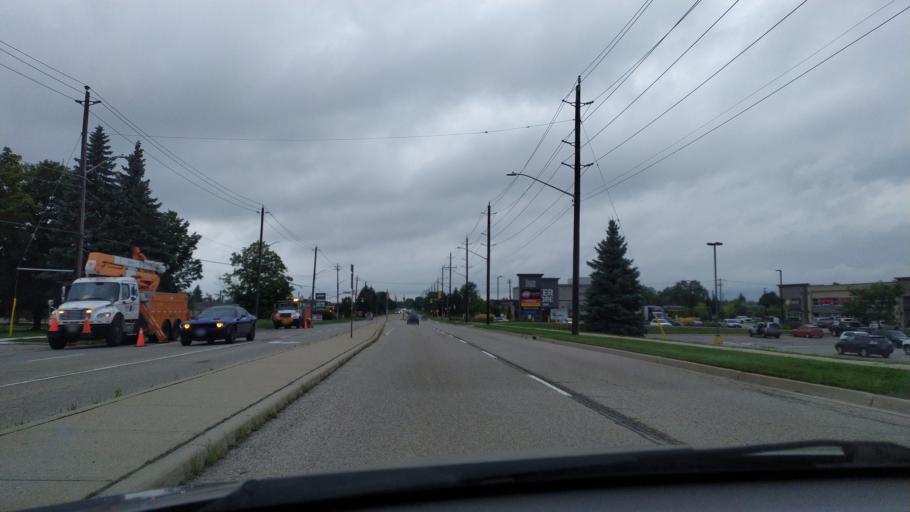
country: CA
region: Ontario
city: Waterloo
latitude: 43.5038
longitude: -80.5357
